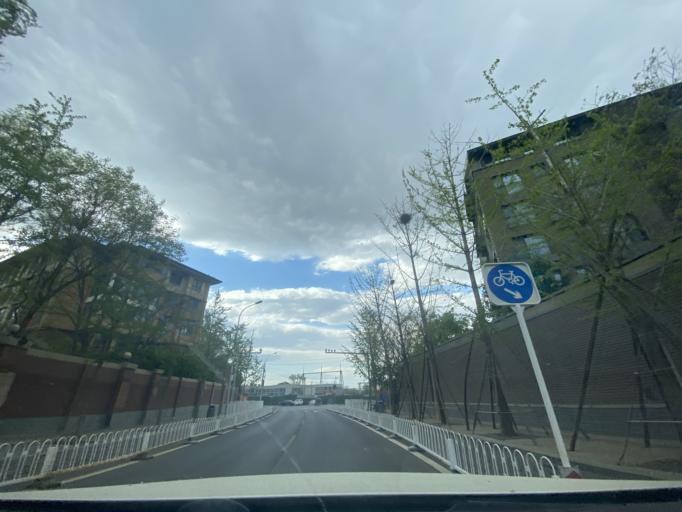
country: CN
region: Beijing
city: Haidian
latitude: 39.9721
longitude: 116.2857
